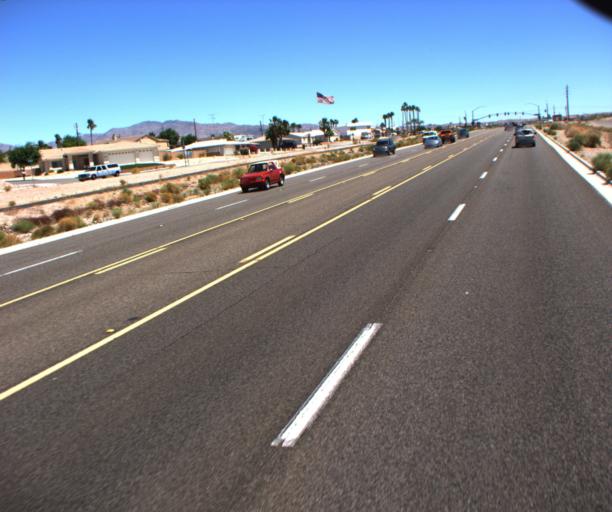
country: US
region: Arizona
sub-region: Mohave County
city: Lake Havasu City
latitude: 34.4539
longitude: -114.3010
